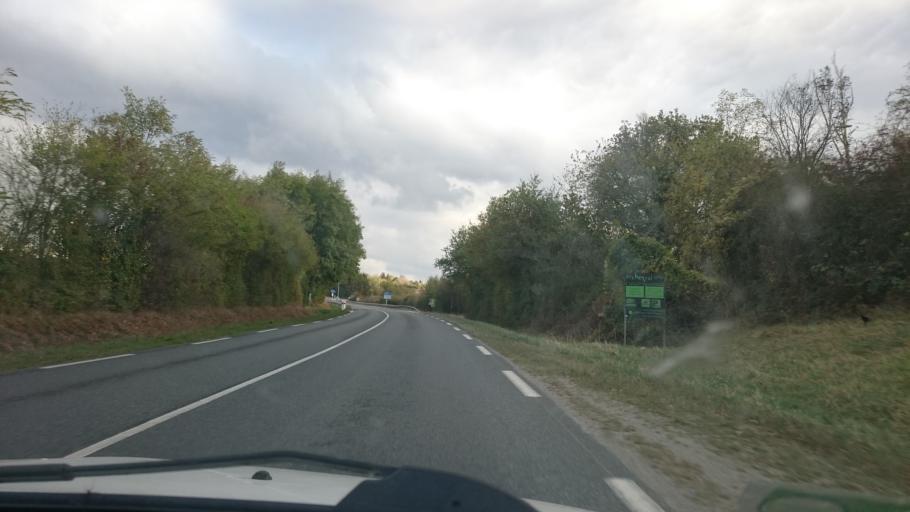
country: FR
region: Centre
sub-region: Departement de l'Indre
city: Saint-Marcel
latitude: 46.6103
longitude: 1.5039
